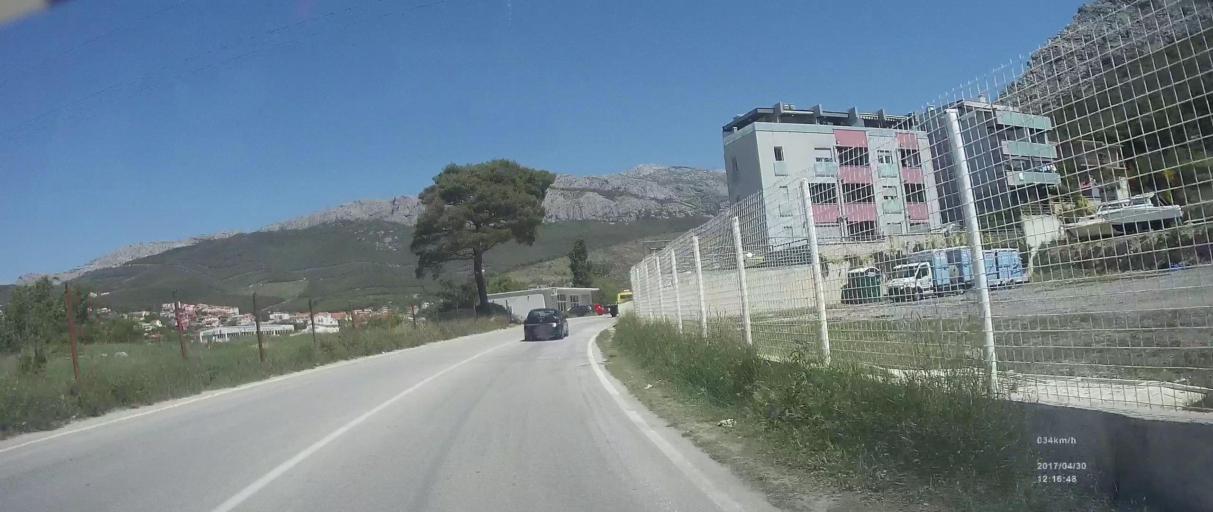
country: HR
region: Splitsko-Dalmatinska
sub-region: Grad Split
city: Stobrec
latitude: 43.5125
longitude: 16.5394
